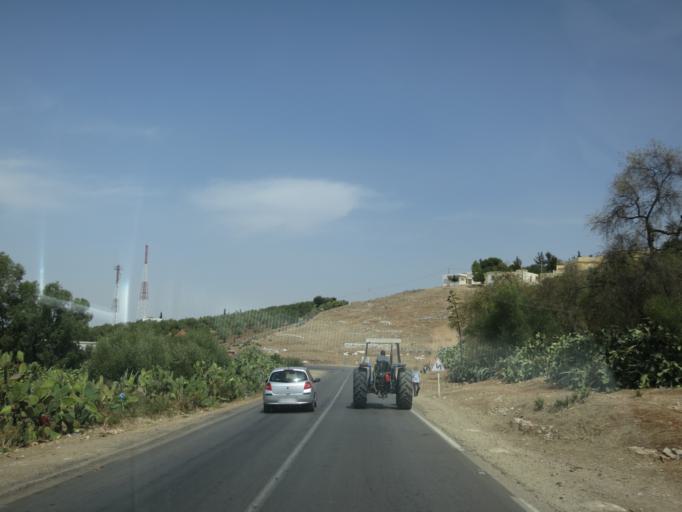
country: MA
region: Meknes-Tafilalet
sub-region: Meknes
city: Meknes
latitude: 34.0380
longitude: -5.5693
